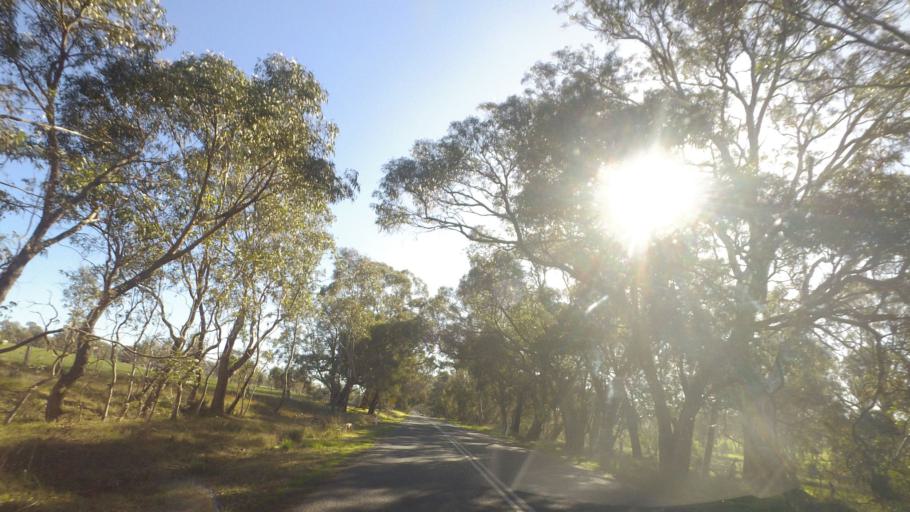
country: AU
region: Victoria
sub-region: Mount Alexander
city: Castlemaine
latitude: -36.9606
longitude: 144.3510
